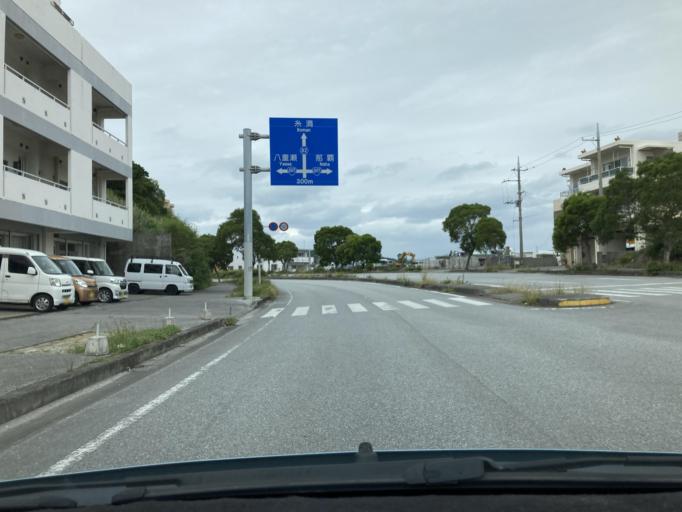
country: JP
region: Okinawa
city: Tomigusuku
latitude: 26.1814
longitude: 127.7189
